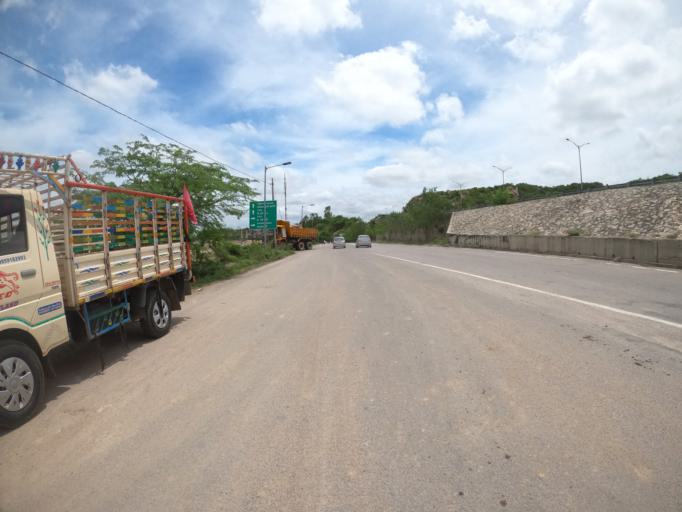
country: IN
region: Telangana
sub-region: Hyderabad
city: Hyderabad
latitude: 17.3078
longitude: 78.3771
